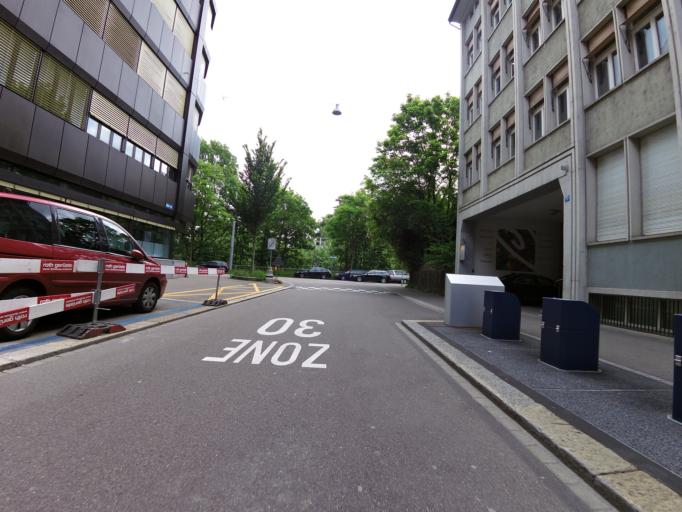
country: CH
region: Zurich
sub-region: Bezirk Zuerich
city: Zuerich (Kreis 4) / Werd
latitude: 47.3704
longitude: 8.5287
